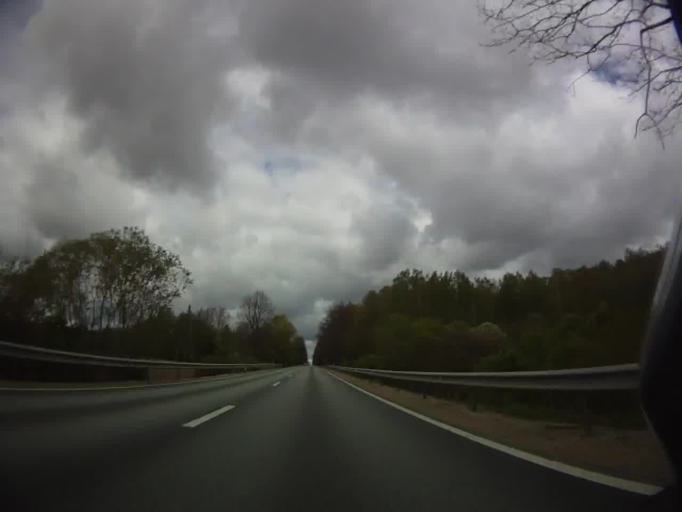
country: LV
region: Krimulda
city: Ragana
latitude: 57.1559
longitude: 24.6881
